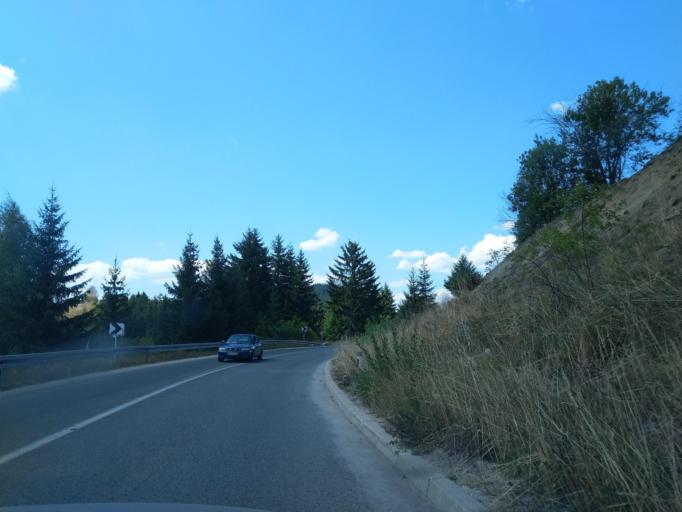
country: RS
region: Central Serbia
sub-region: Zlatiborski Okrug
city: Nova Varos
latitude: 43.4285
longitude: 19.8293
